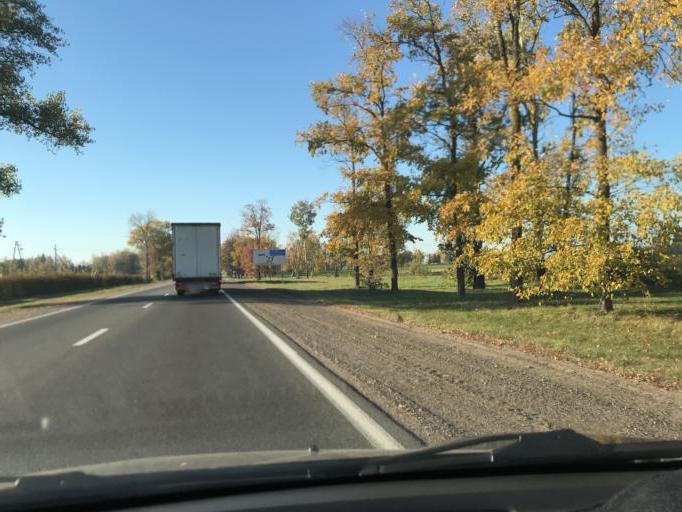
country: BY
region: Minsk
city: Slutsk
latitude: 53.0504
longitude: 27.5598
